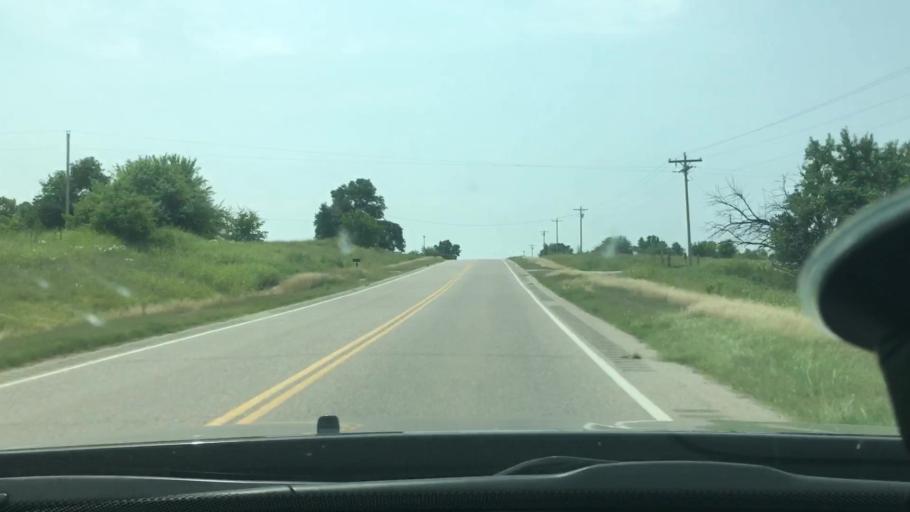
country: US
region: Oklahoma
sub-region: Marshall County
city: Kingston
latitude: 34.0353
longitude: -96.7611
